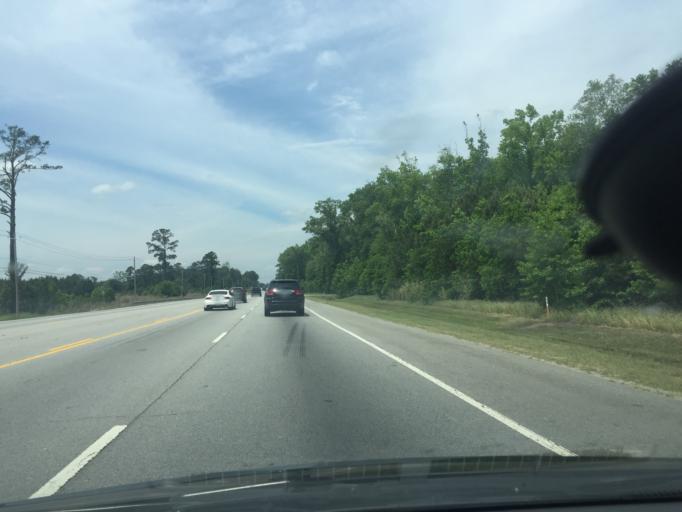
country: US
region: Georgia
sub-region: Chatham County
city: Bloomingdale
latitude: 32.1369
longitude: -81.3128
